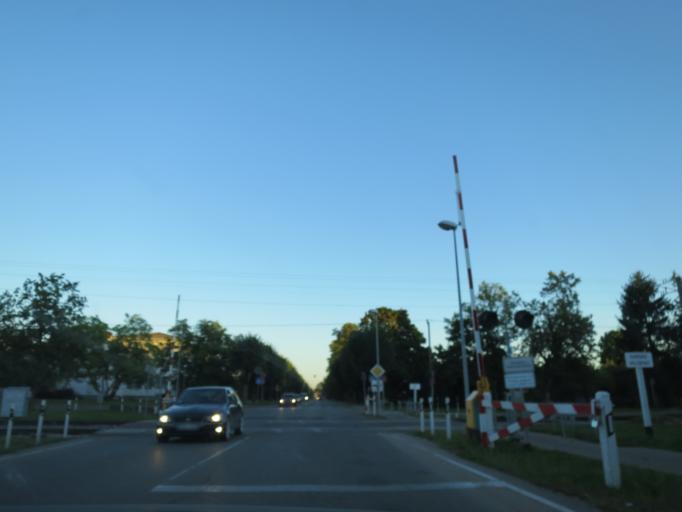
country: LV
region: Sigulda
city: Sigulda
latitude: 57.1521
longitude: 24.8468
